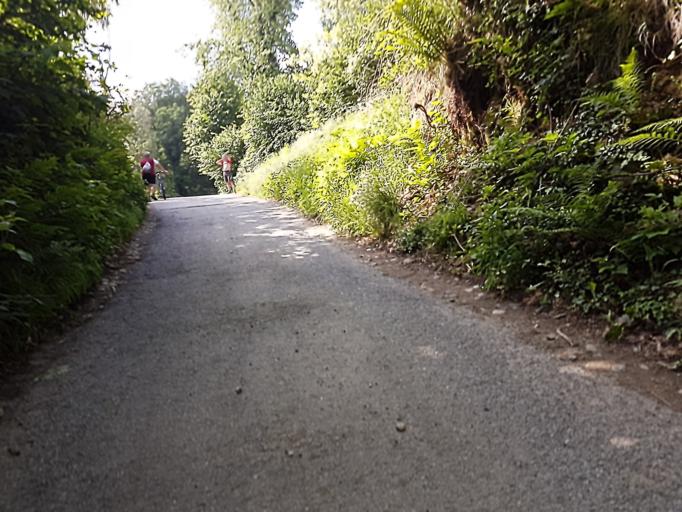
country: IT
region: Piedmont
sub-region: Provincia di Torino
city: Vialfre
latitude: 45.3799
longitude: 7.8260
